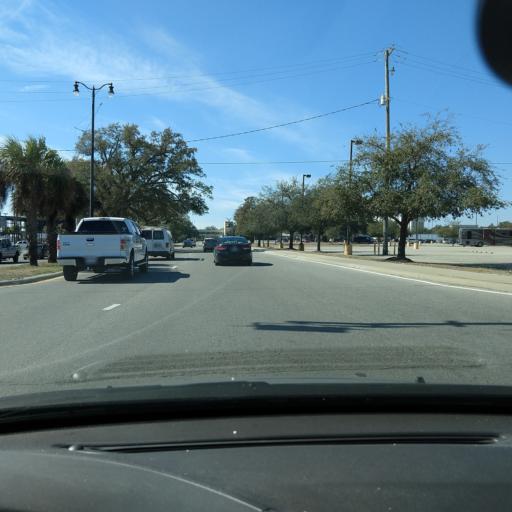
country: US
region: Mississippi
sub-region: Harrison County
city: Gulfport
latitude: 30.3643
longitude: -89.0978
